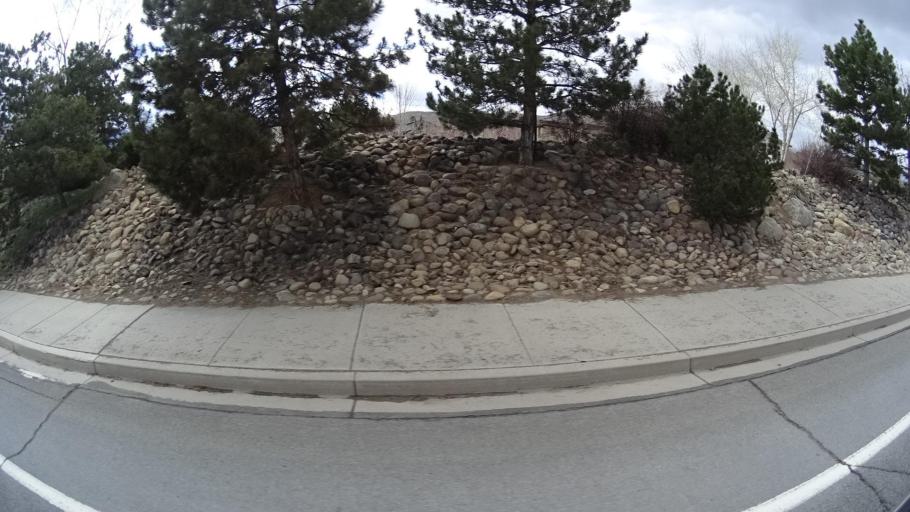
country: US
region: Nevada
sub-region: Washoe County
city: Sparks
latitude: 39.4041
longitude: -119.7692
